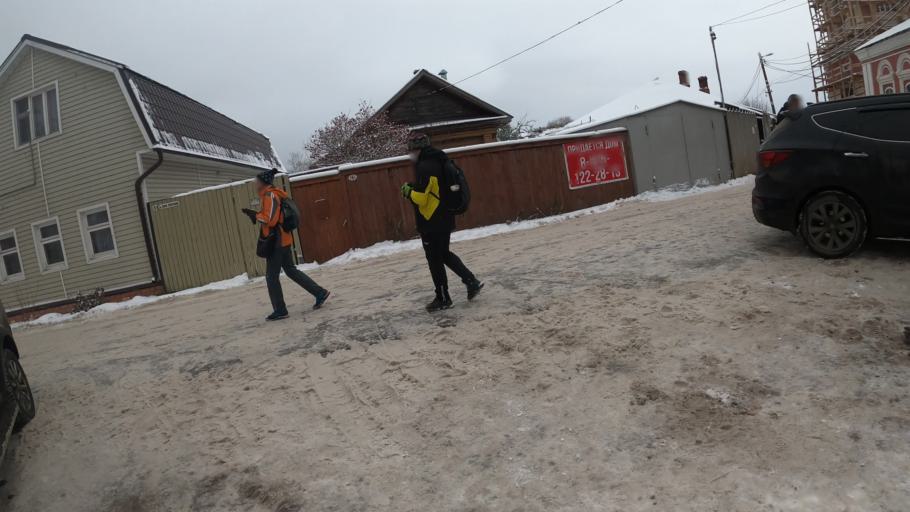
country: RU
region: Jaroslavl
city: Pereslavl'-Zalesskiy
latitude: 56.7351
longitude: 38.8290
